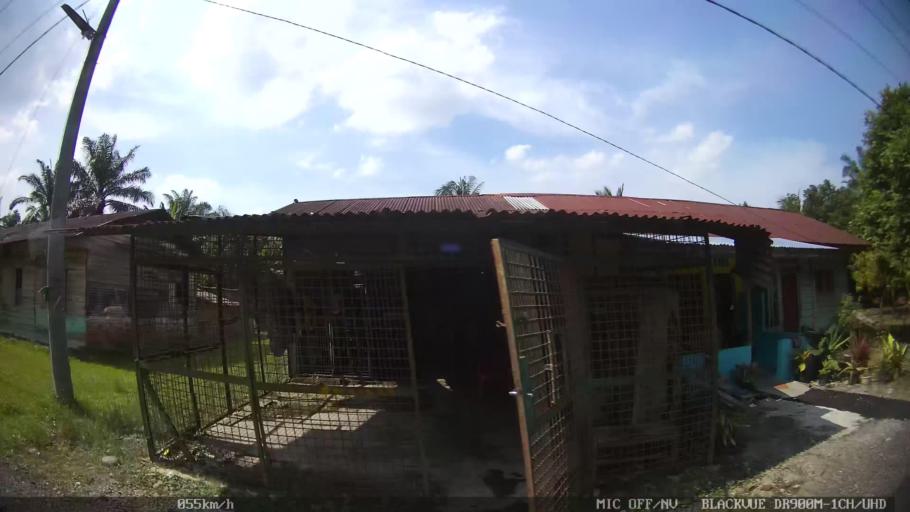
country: ID
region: North Sumatra
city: Binjai
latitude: 3.6345
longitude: 98.5242
